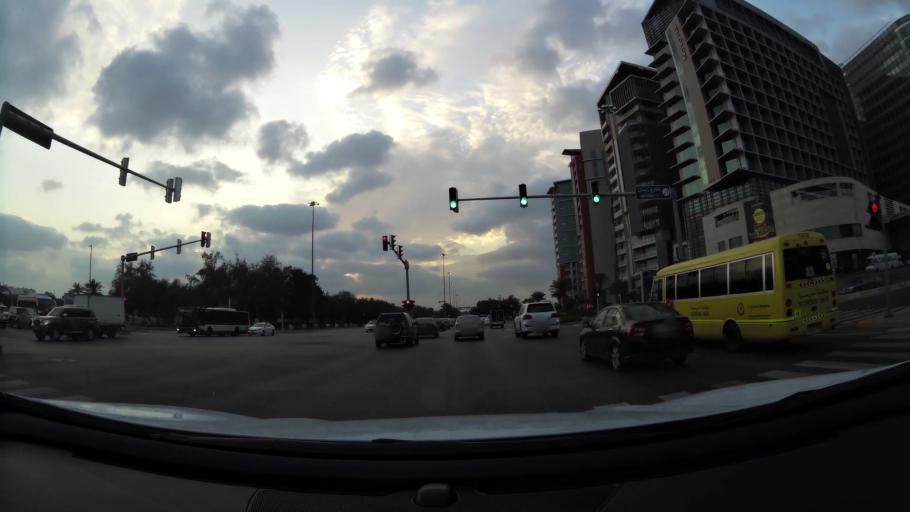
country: AE
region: Abu Dhabi
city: Abu Dhabi
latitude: 24.4287
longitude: 54.4295
